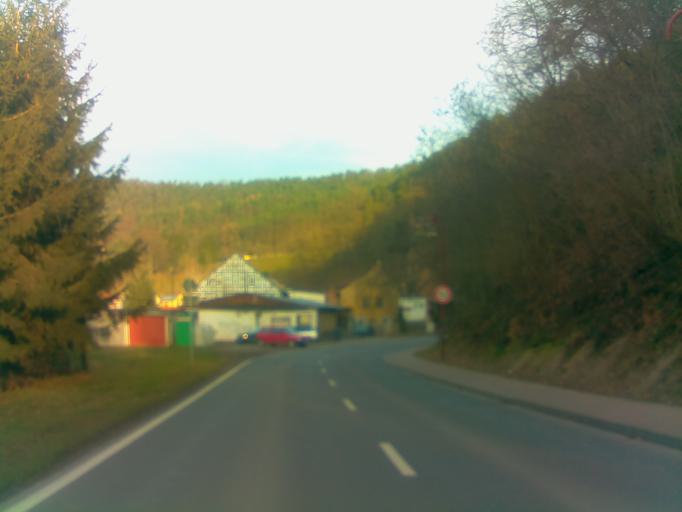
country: DE
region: Thuringia
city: Langenorla
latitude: 50.7358
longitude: 11.5946
